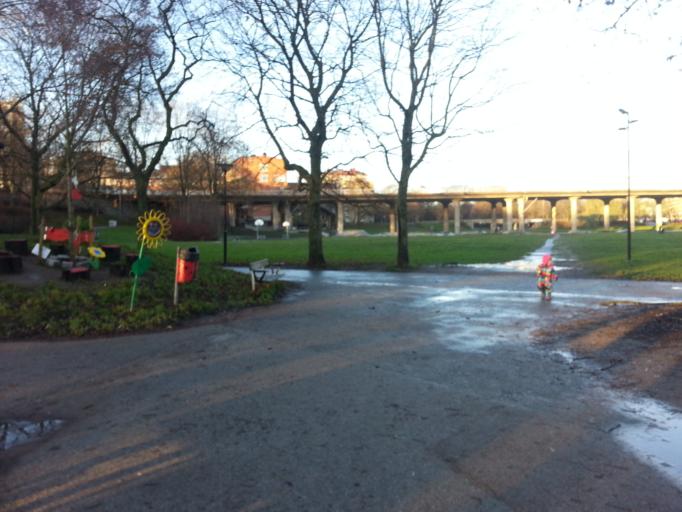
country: SE
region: Stockholm
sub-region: Solna Kommun
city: Solna
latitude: 59.3286
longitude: 18.0243
